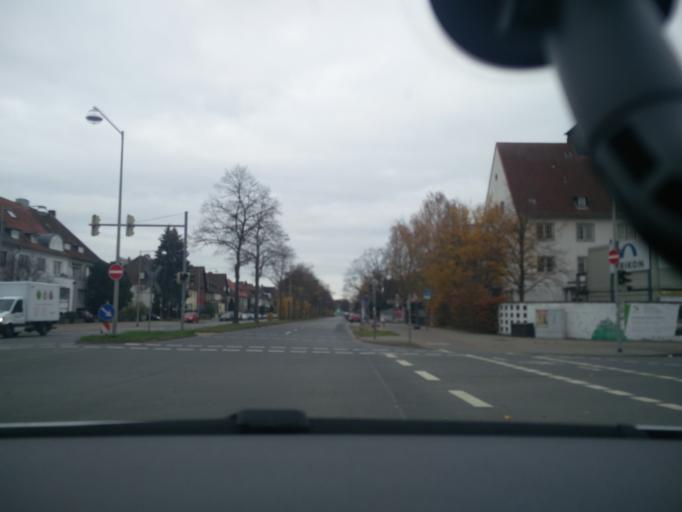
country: DE
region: Lower Saxony
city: Hannover
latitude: 52.3649
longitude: 9.7723
